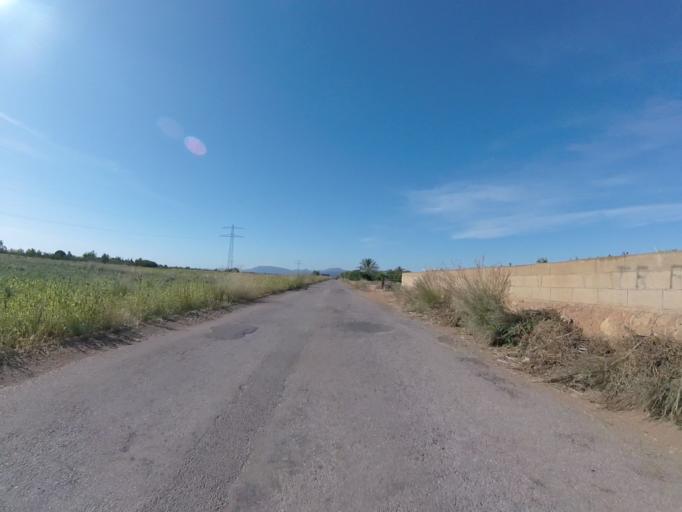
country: ES
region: Valencia
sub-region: Provincia de Castello
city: Torreblanca
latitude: 40.2166
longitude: 0.2187
